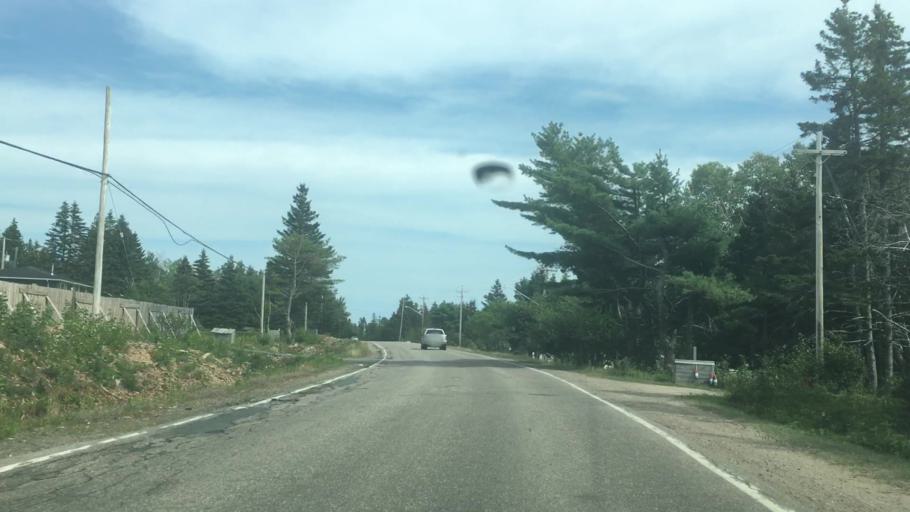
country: CA
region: Nova Scotia
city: Sydney Mines
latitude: 46.6898
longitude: -60.3917
